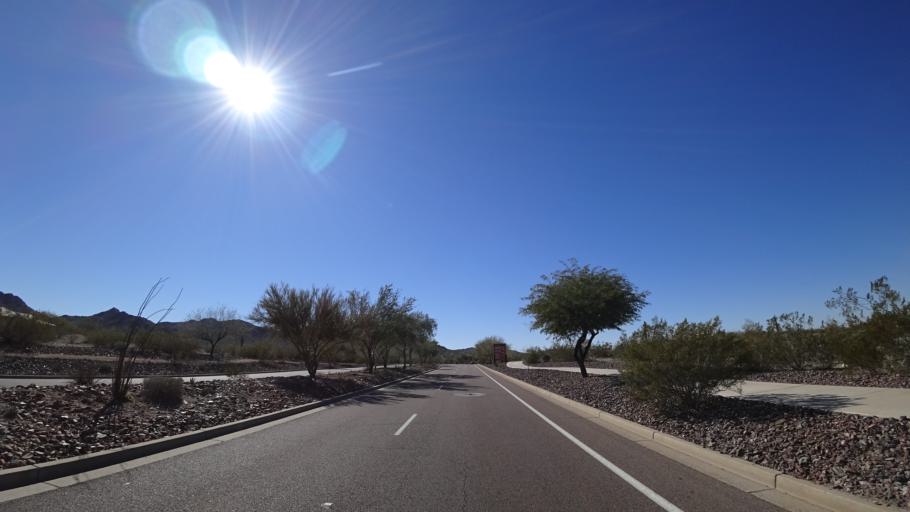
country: US
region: Arizona
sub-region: Maricopa County
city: Goodyear
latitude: 33.3677
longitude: -112.4041
